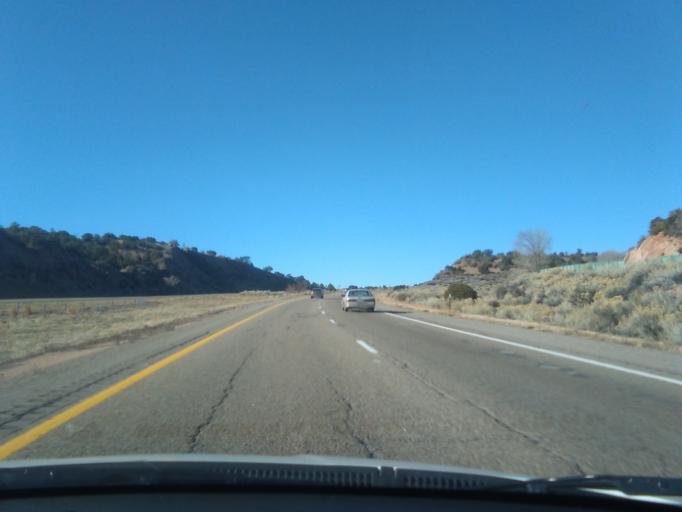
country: US
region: New Mexico
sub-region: Santa Fe County
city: Eldorado at Santa Fe
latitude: 35.5377
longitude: -105.8517
